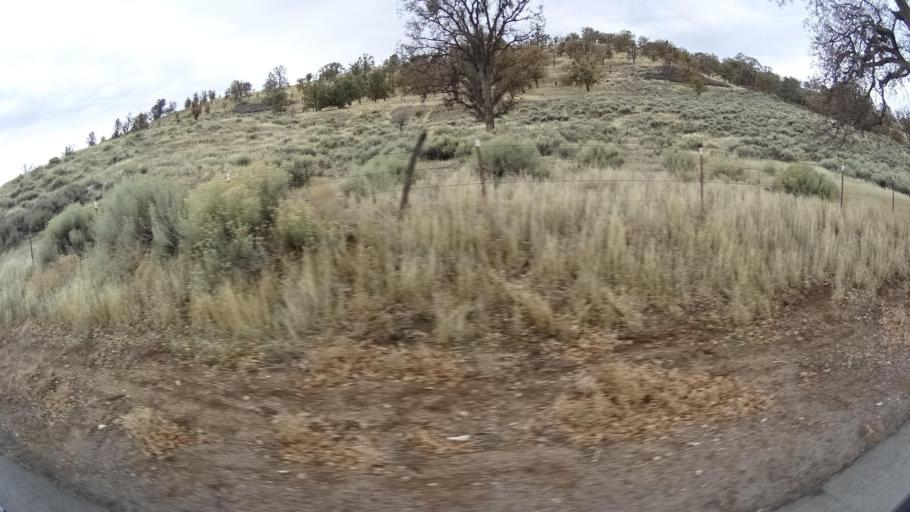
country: US
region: California
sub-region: Kern County
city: Golden Hills
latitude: 35.1214
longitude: -118.5516
